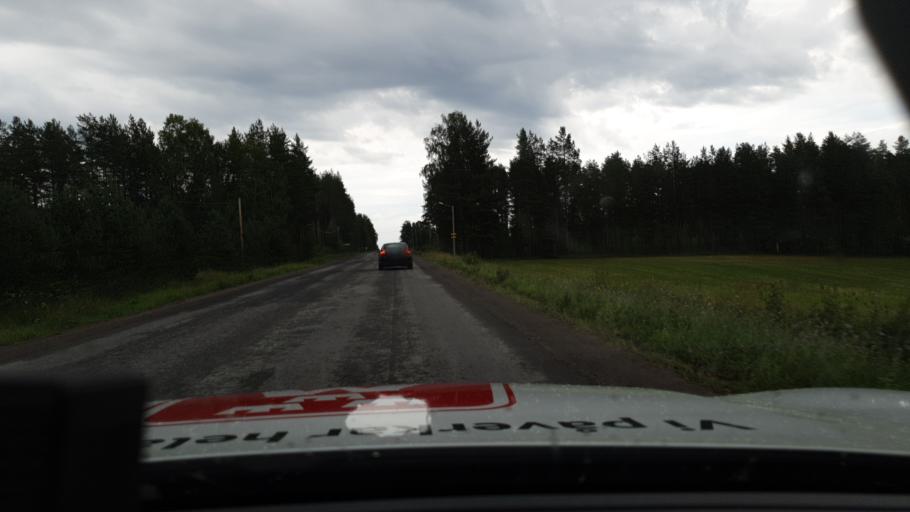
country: SE
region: Norrbotten
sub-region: Bodens Kommun
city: Boden
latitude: 65.8574
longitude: 21.4690
